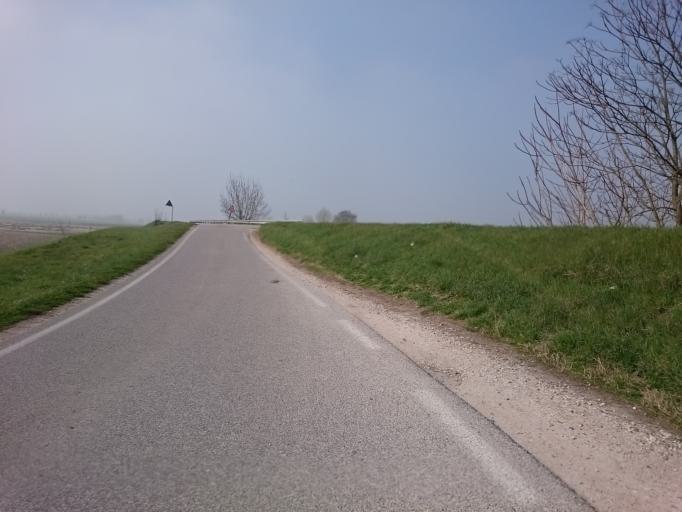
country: IT
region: Veneto
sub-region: Provincia di Padova
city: Due Carrare
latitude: 45.2723
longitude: 11.8247
